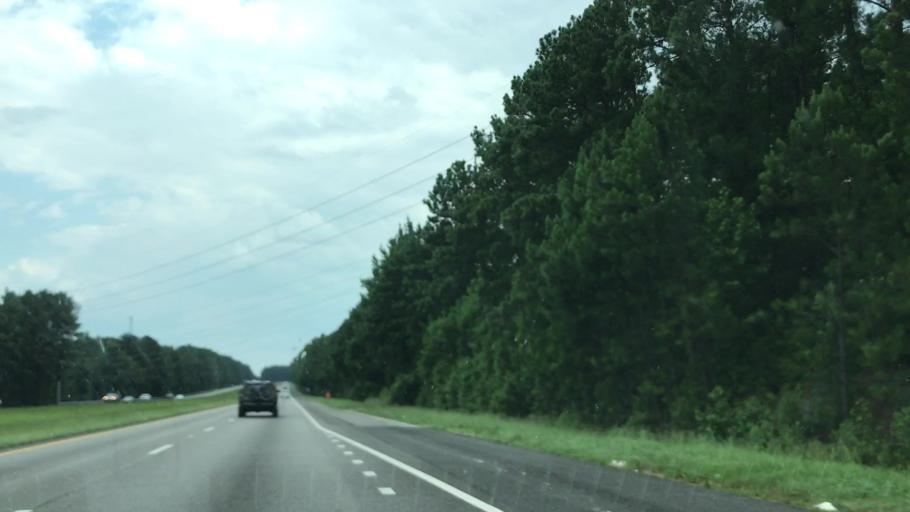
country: US
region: South Carolina
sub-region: Richland County
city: Blythewood
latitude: 34.2748
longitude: -80.9978
